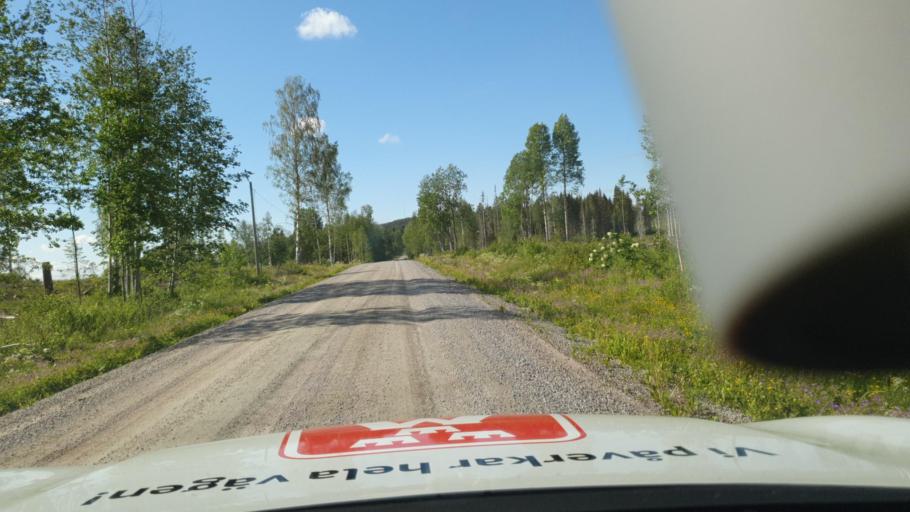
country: SE
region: Vaesterbotten
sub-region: Vannas Kommun
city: Vaennaes
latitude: 63.7794
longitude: 19.6364
